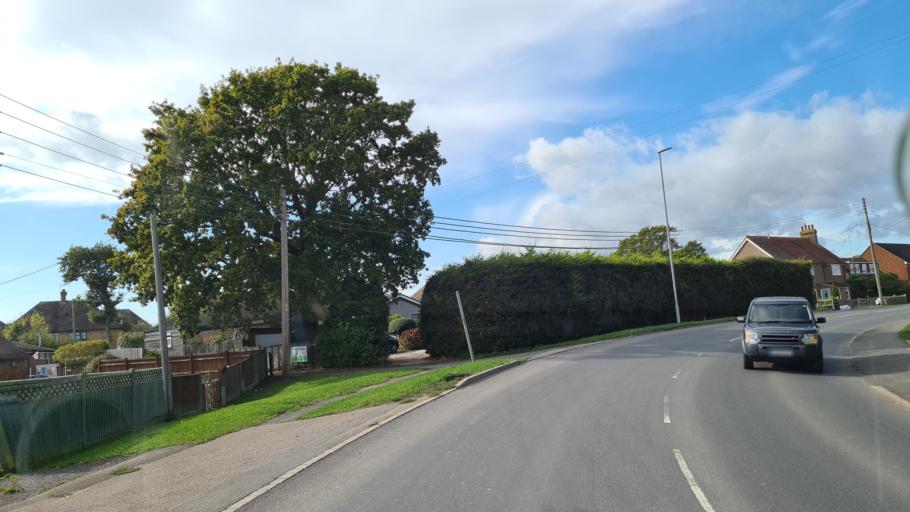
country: GB
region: England
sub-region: East Sussex
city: Hailsham
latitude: 50.8766
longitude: 0.2616
